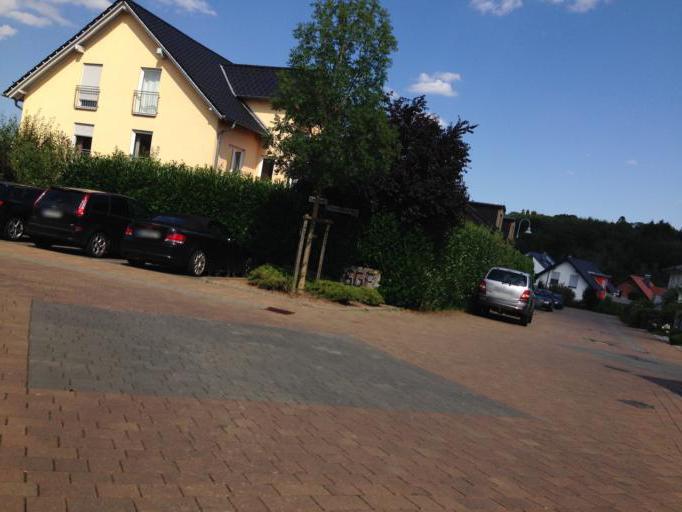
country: DE
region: Hesse
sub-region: Regierungsbezirk Giessen
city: Heuchelheim
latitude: 50.6252
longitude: 8.6408
